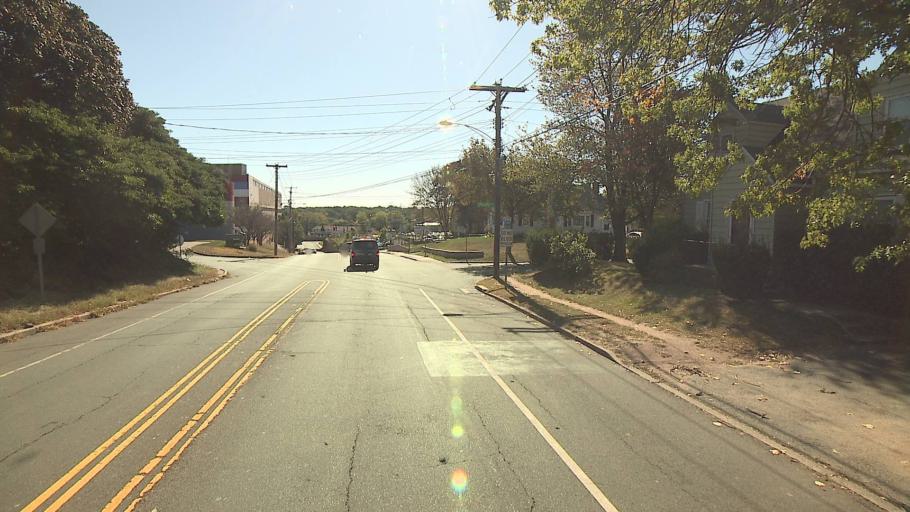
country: US
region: Connecticut
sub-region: New Haven County
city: West Haven
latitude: 41.2732
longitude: -72.9632
